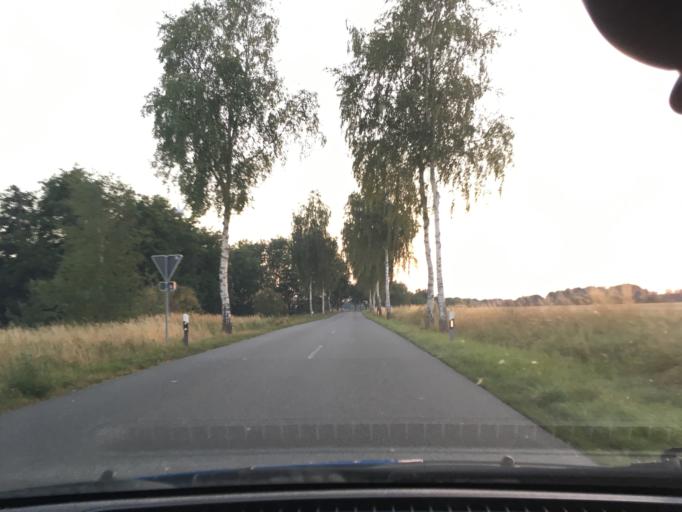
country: DE
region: Lower Saxony
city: Barnstedt
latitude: 53.1367
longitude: 10.4006
